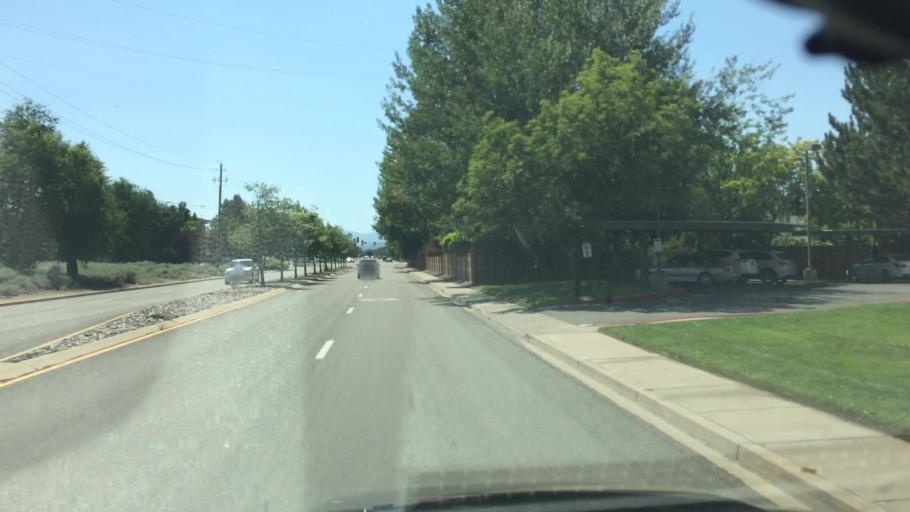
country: US
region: Nevada
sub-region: Washoe County
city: Sparks
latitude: 39.5420
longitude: -119.7081
